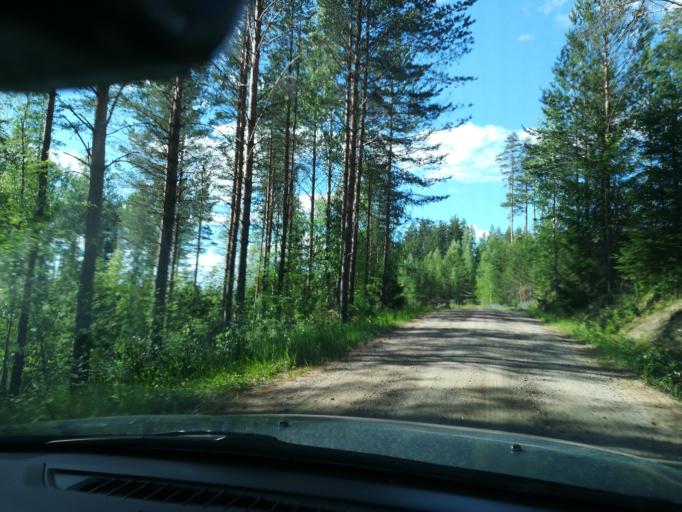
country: FI
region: Southern Savonia
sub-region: Mikkeli
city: Puumala
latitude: 61.6596
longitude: 28.1603
